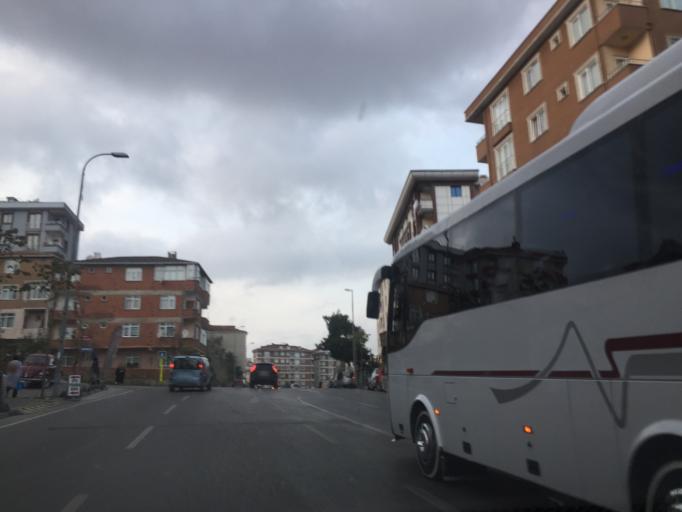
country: TR
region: Istanbul
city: Samandira
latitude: 40.9878
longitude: 29.2319
